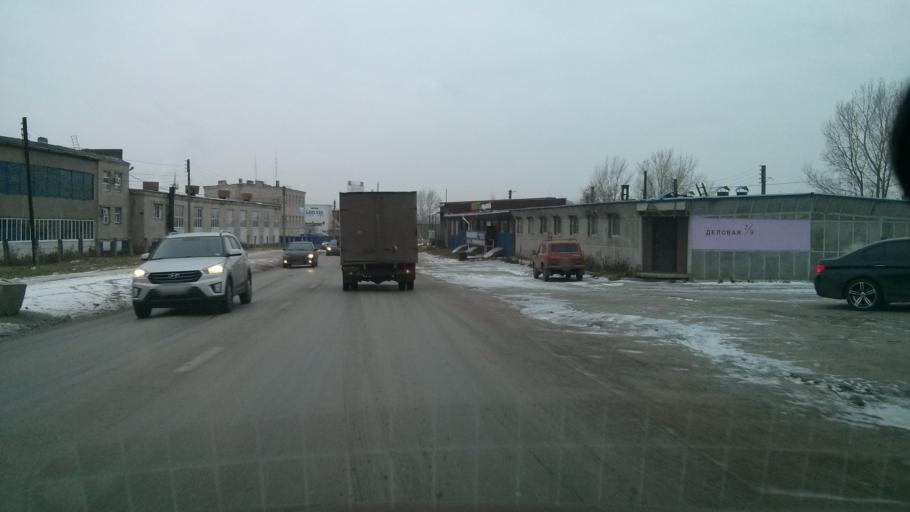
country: RU
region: Nizjnij Novgorod
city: Bor
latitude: 56.3070
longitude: 44.0597
